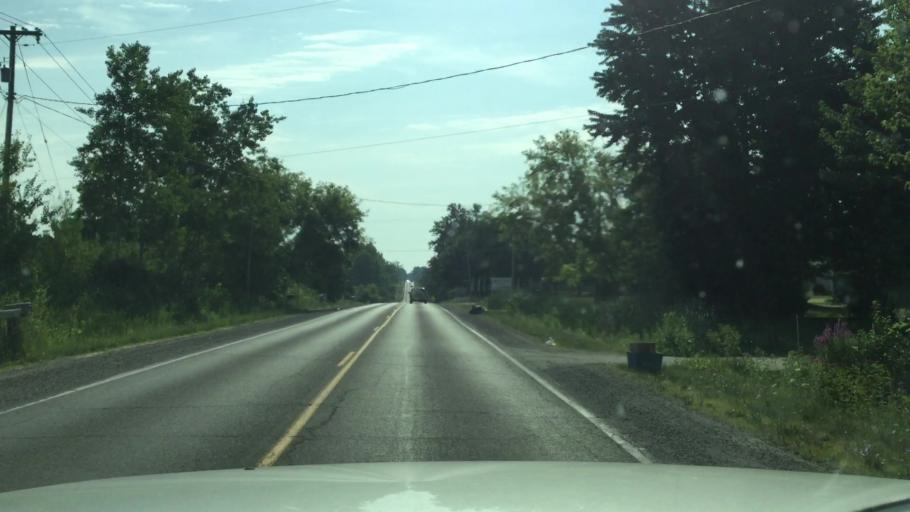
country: US
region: Michigan
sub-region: Genesee County
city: Flushing
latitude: 43.1177
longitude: -83.8647
